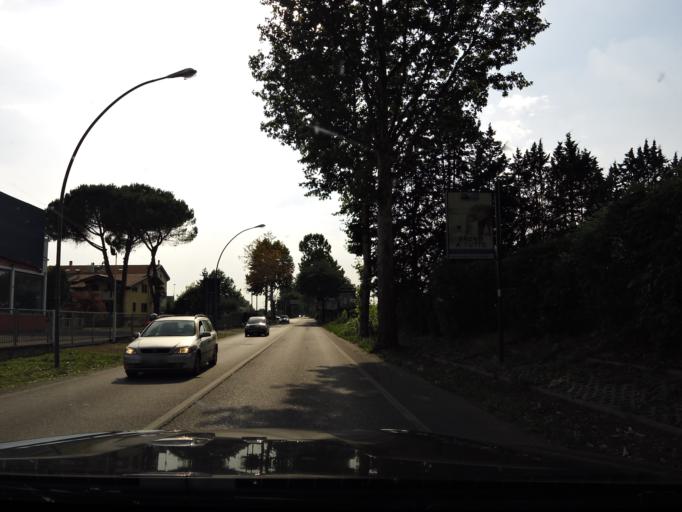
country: IT
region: Veneto
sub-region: Provincia di Verona
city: Parona
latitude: 45.4467
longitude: 10.9396
